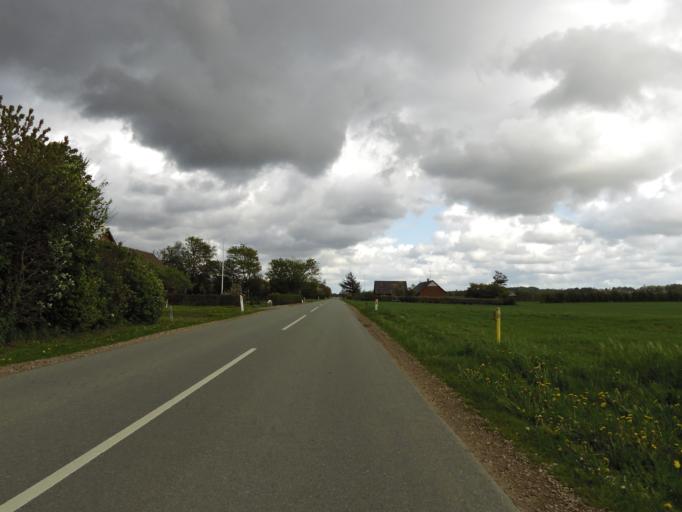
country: DK
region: South Denmark
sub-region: Haderslev Kommune
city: Gram
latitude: 55.3025
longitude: 9.0348
